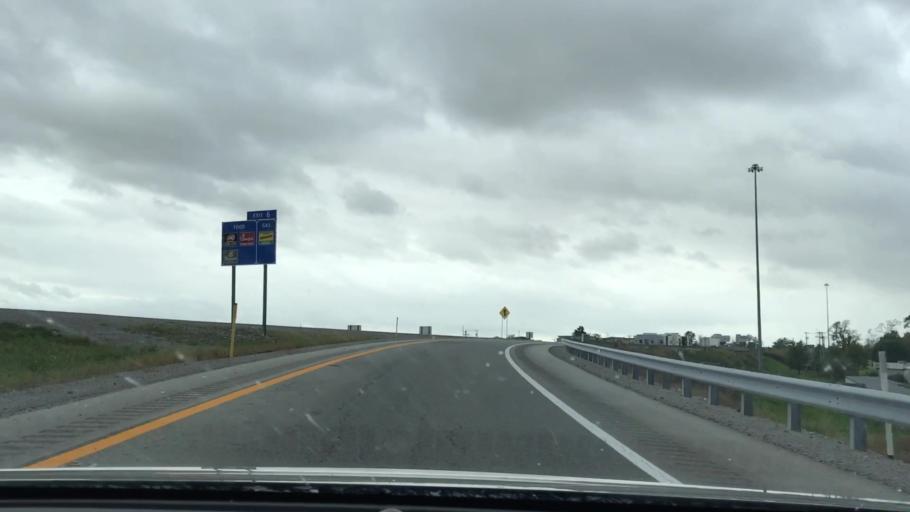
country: US
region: Kentucky
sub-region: Christian County
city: Hopkinsville
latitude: 36.8301
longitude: -87.4753
